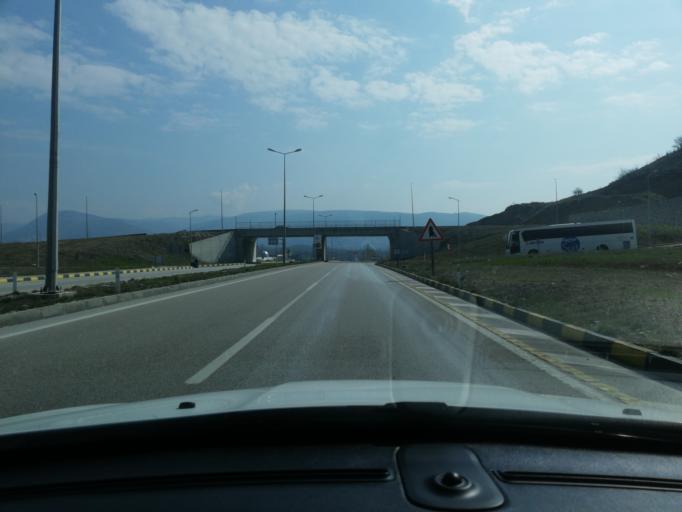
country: TR
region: Cankiri
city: Ilgaz
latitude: 40.9074
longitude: 33.6208
